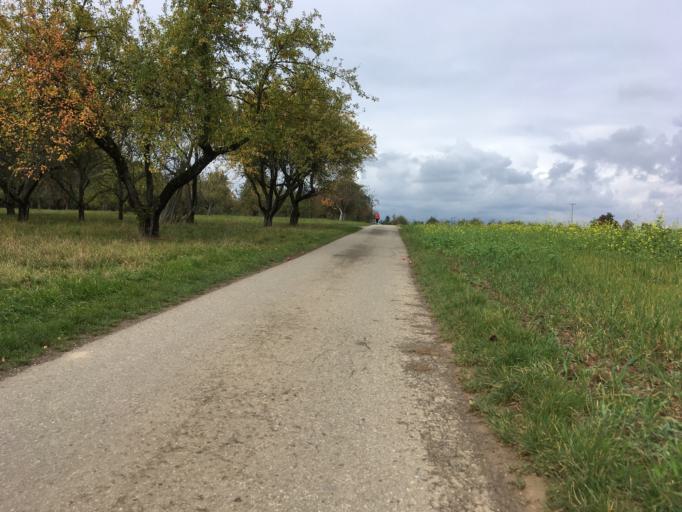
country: DE
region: Baden-Wuerttemberg
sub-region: Tuebingen Region
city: Gomaringen
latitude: 48.4887
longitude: 9.0943
